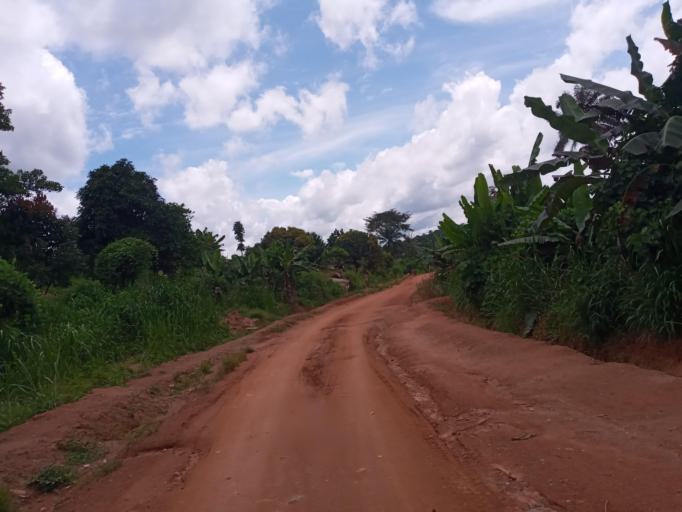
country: SL
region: Eastern Province
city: Koidu
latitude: 8.6455
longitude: -10.9242
